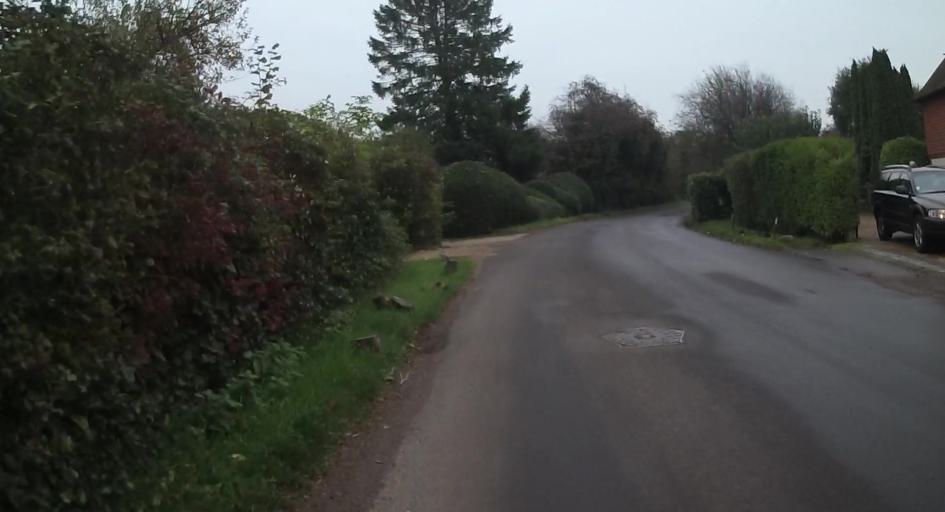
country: GB
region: England
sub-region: Hampshire
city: Long Sutton
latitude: 51.1905
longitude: -0.9062
